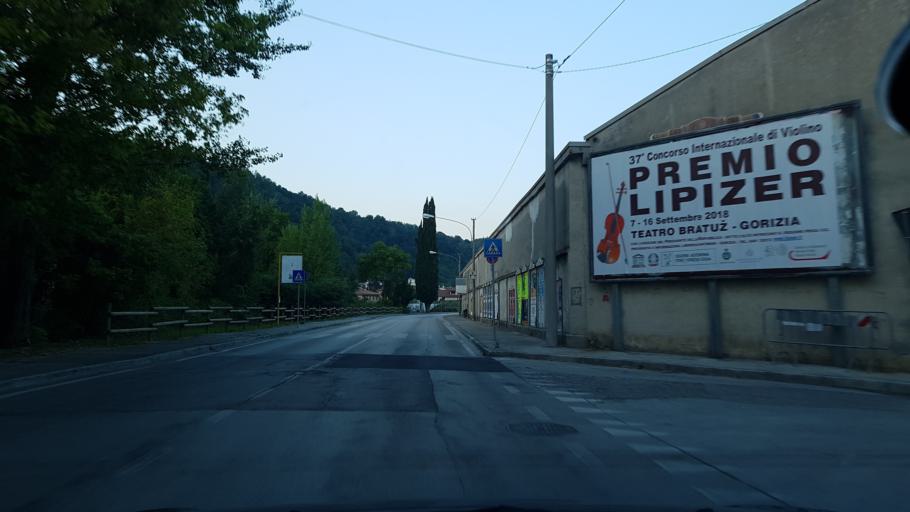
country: IT
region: Friuli Venezia Giulia
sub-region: Provincia di Gorizia
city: Gorizia
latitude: 45.9438
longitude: 13.5992
